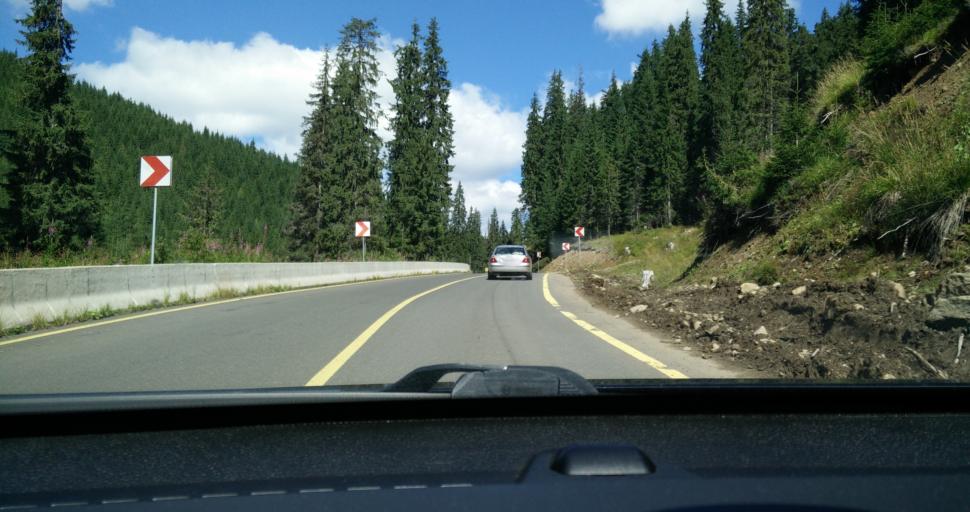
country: RO
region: Hunedoara
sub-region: Oras Petrila
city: Petrila
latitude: 45.4411
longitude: 23.6266
